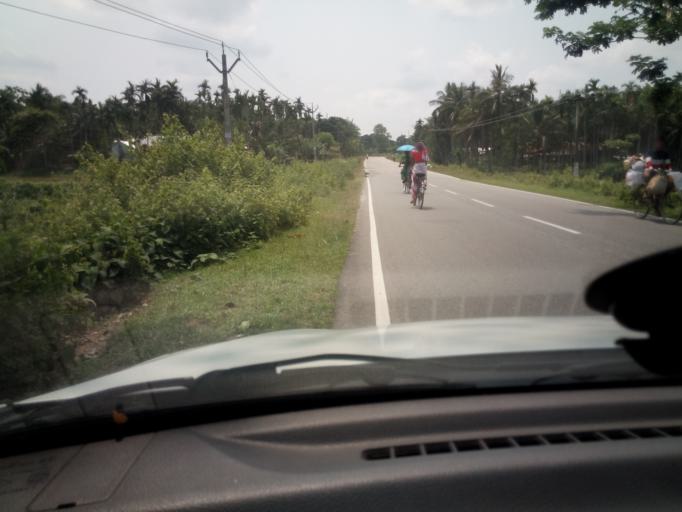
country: IN
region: Assam
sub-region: Udalguri
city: Udalguri
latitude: 26.7213
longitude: 92.1933
